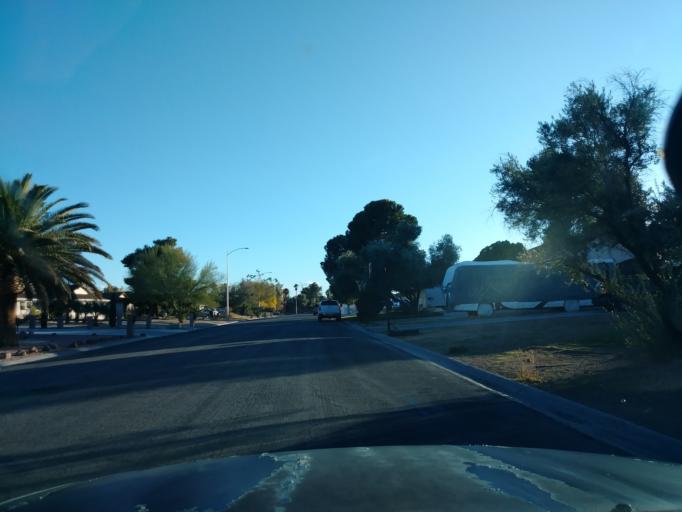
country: US
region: Nevada
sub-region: Clark County
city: Spring Valley
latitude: 36.1511
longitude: -115.2403
